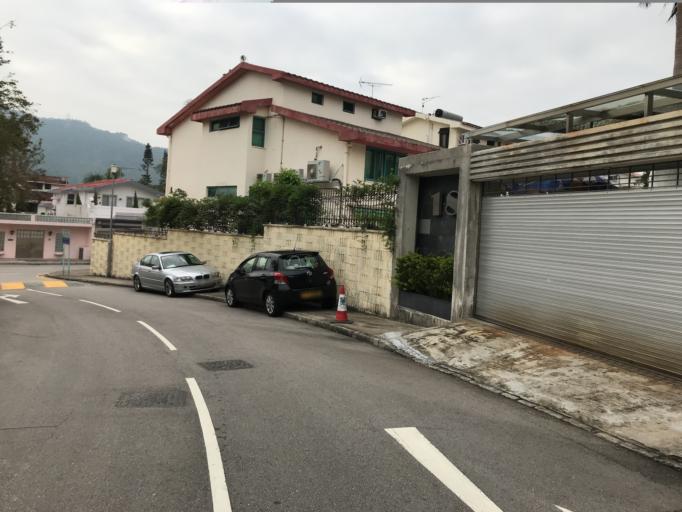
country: HK
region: Tai Po
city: Tai Po
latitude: 22.4641
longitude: 114.1560
